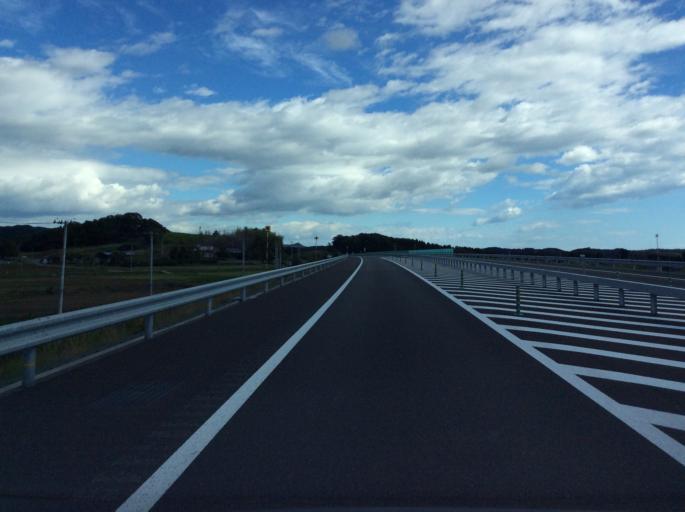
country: JP
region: Fukushima
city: Namie
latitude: 37.6183
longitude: 140.9278
